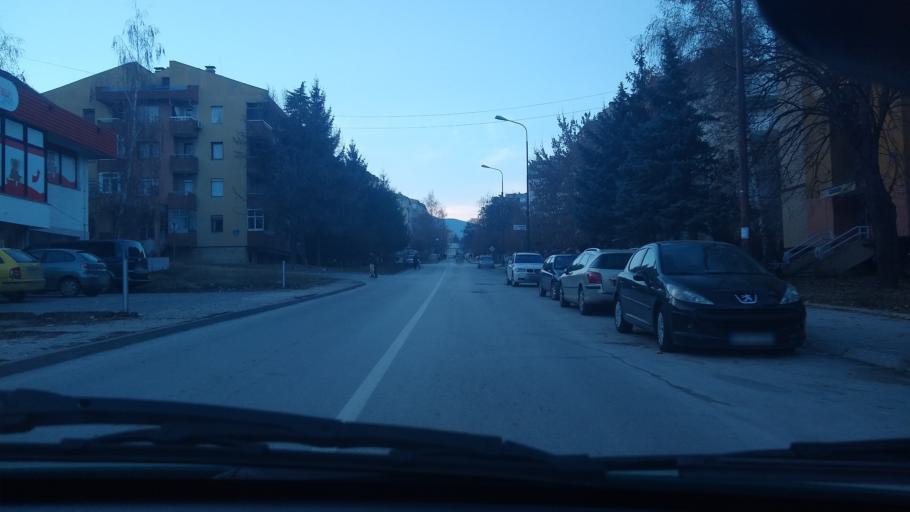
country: MK
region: Bitola
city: Bitola
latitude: 41.0233
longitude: 21.3136
